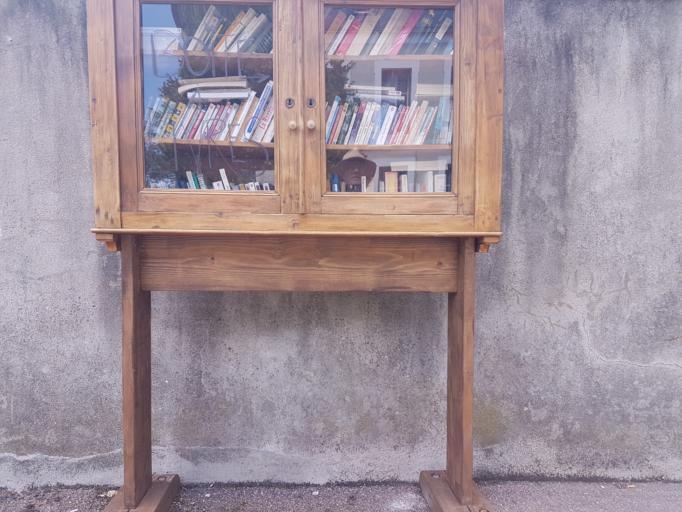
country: FR
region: Bourgogne
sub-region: Departement de la Nievre
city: Clamecy
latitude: 47.4596
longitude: 3.5207
